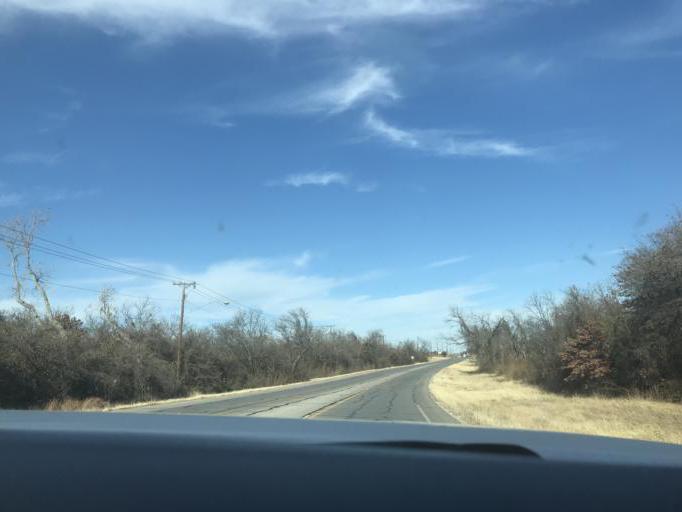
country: US
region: Texas
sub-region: Erath County
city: Stephenville
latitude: 32.2112
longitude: -98.2464
